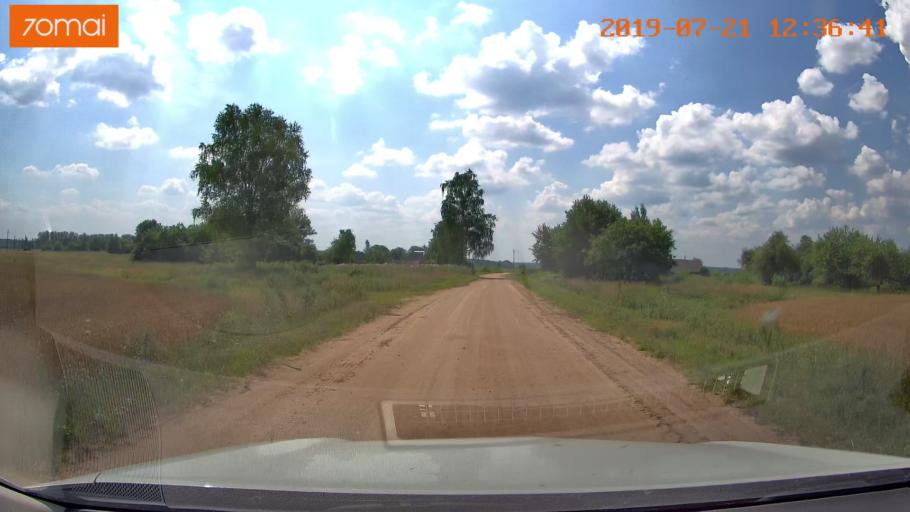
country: BY
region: Grodnenskaya
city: Lyubcha
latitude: 53.8681
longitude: 26.0027
